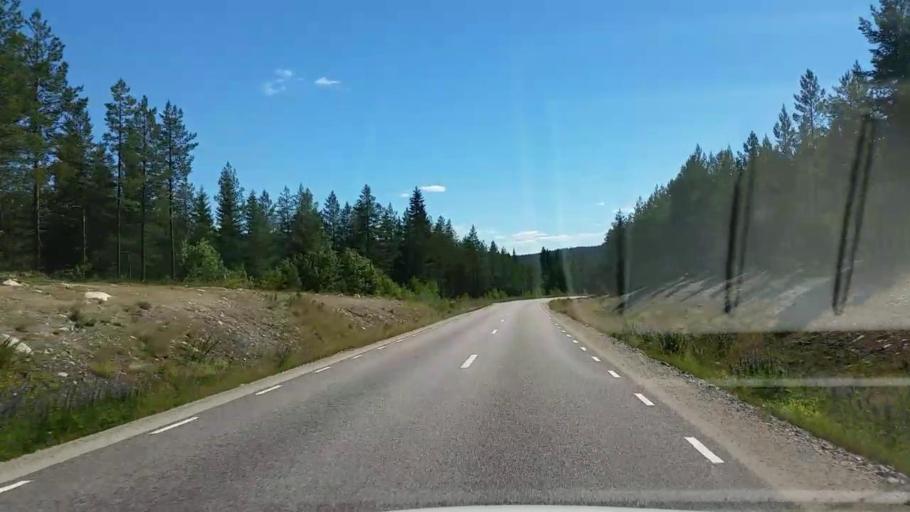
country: SE
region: Gaevleborg
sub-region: Ovanakers Kommun
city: Edsbyn
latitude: 61.4340
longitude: 15.7189
